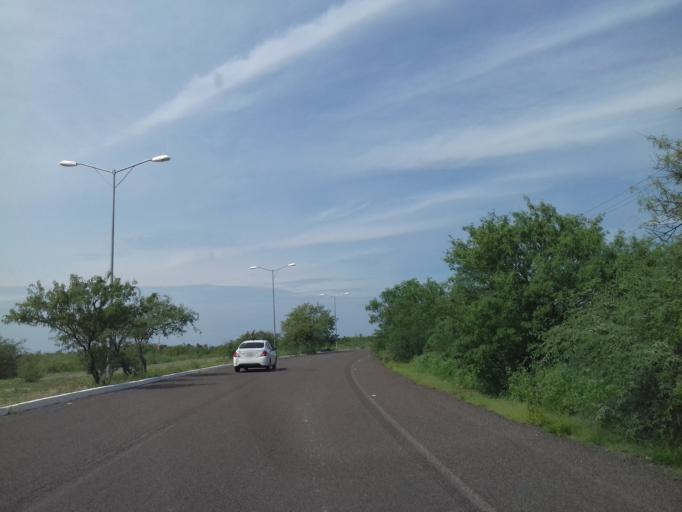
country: MX
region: Sonora
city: Heroica Guaymas
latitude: 27.9702
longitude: -111.1058
